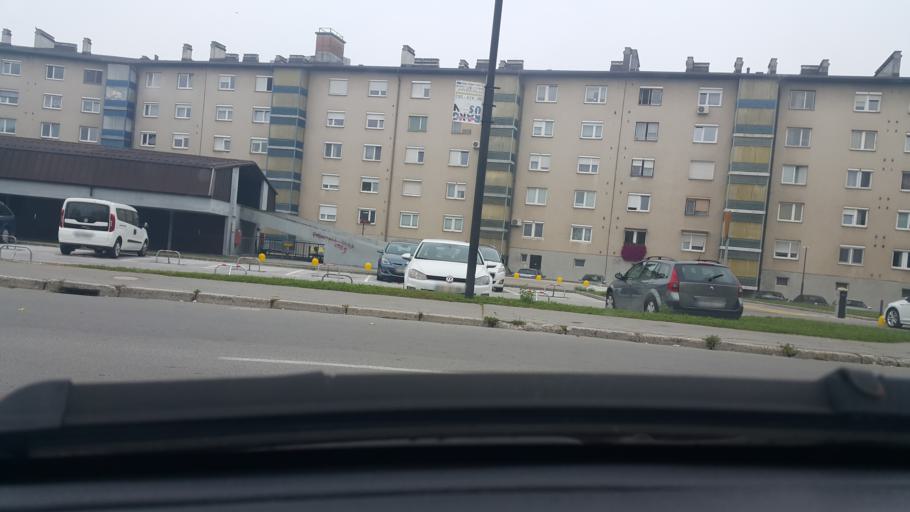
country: SI
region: Ljubljana
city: Ljubljana
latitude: 46.0709
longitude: 14.5457
